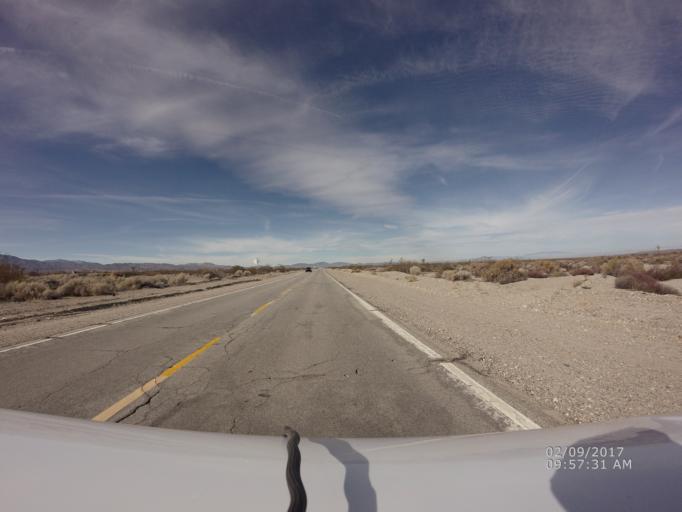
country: US
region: California
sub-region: Los Angeles County
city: Lake Los Angeles
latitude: 34.5425
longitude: -117.8525
